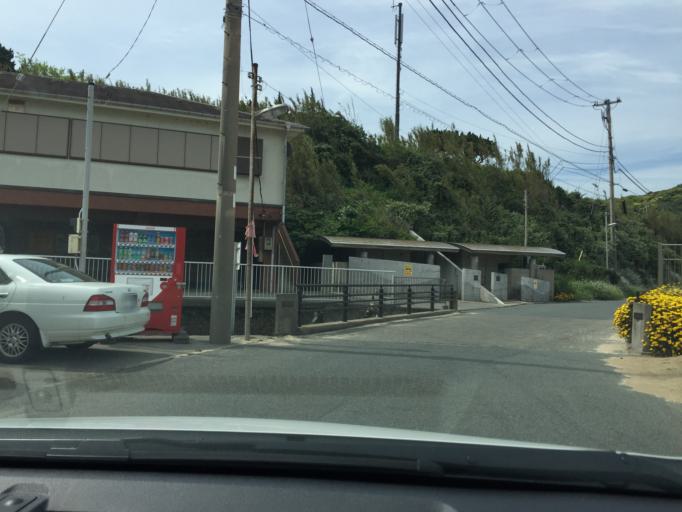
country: JP
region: Shizuoka
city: Shimoda
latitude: 34.6781
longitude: 138.9717
